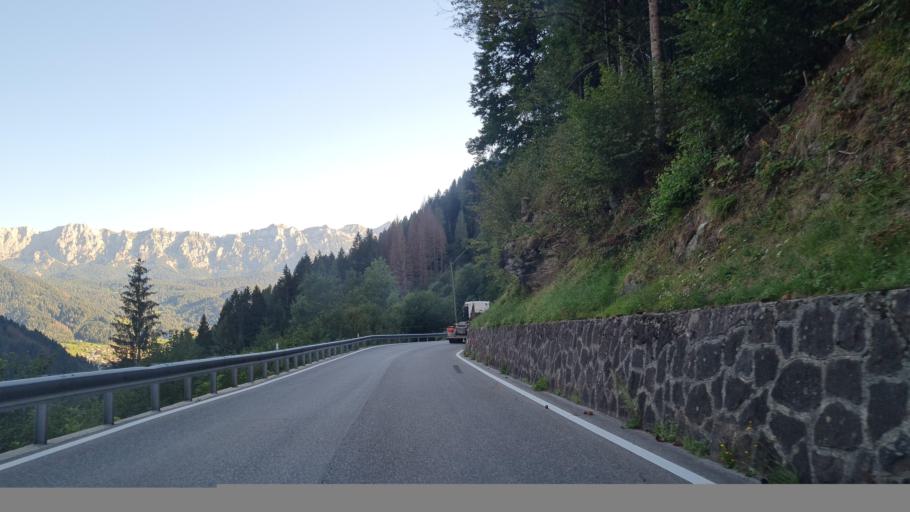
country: IT
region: Trentino-Alto Adige
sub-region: Provincia di Trento
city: Siror
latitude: 46.2092
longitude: 11.8175
